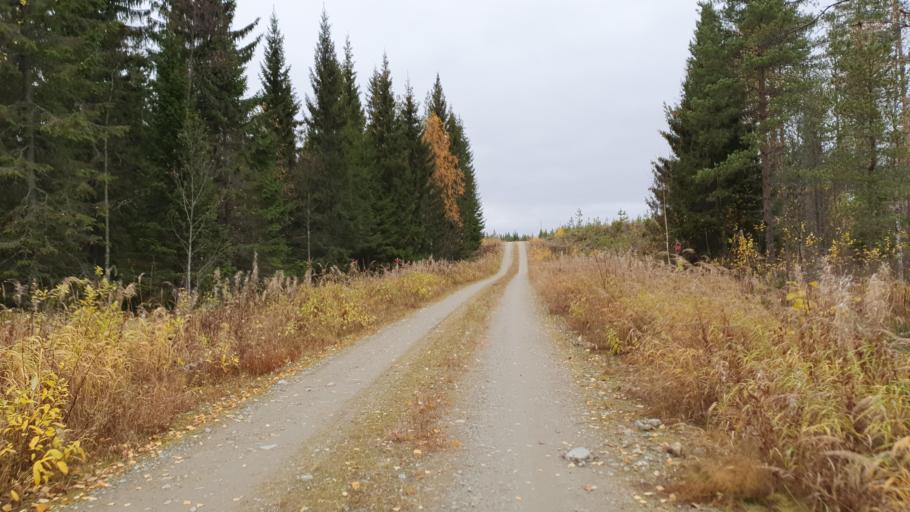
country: FI
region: Kainuu
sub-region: Kehys-Kainuu
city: Kuhmo
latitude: 64.4460
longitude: 29.6232
